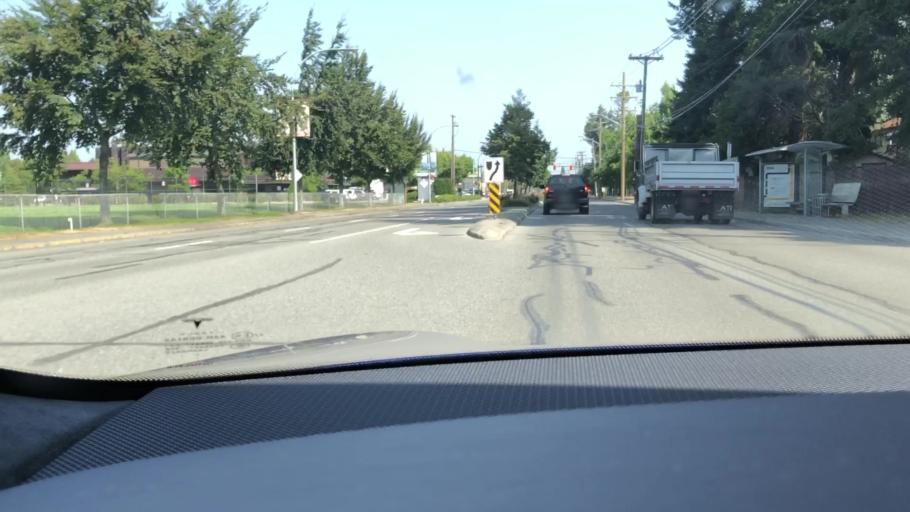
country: US
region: Washington
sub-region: Whatcom County
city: Point Roberts
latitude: 49.0211
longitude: -123.0686
